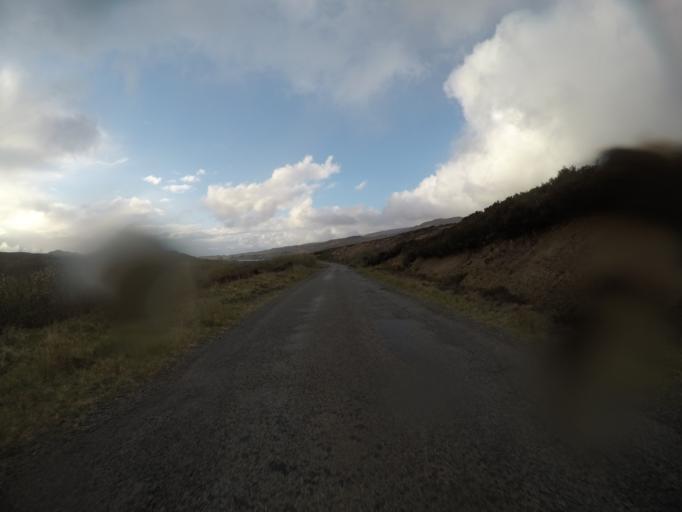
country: GB
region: Scotland
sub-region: Highland
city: Isle of Skye
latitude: 57.4679
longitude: -6.2988
